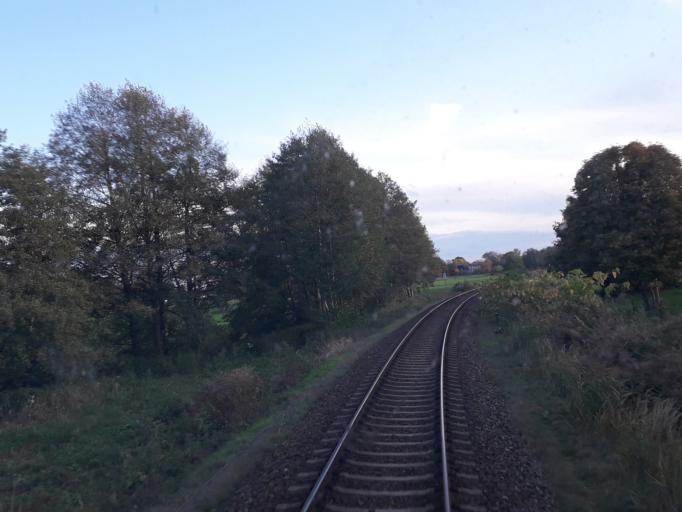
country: DE
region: Brandenburg
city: Wittstock
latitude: 53.1533
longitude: 12.4891
